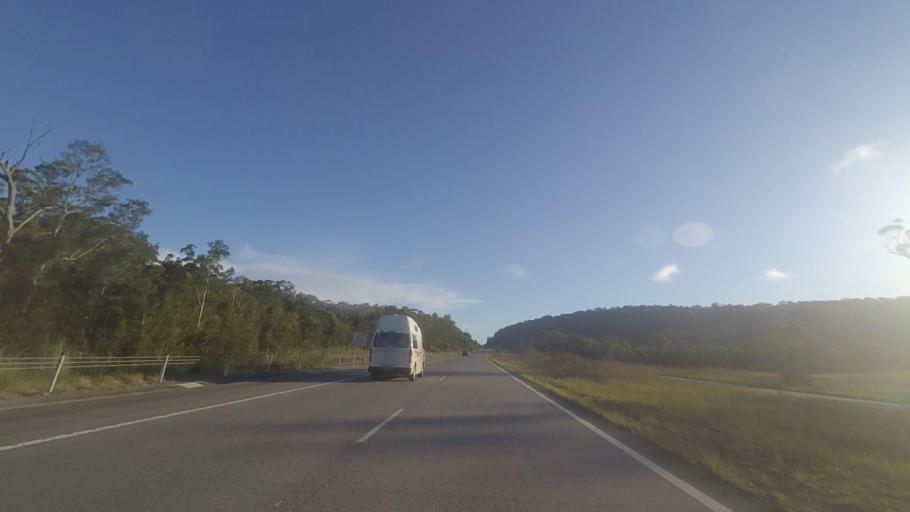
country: AU
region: New South Wales
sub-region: Great Lakes
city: Bulahdelah
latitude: -32.4624
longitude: 152.1972
